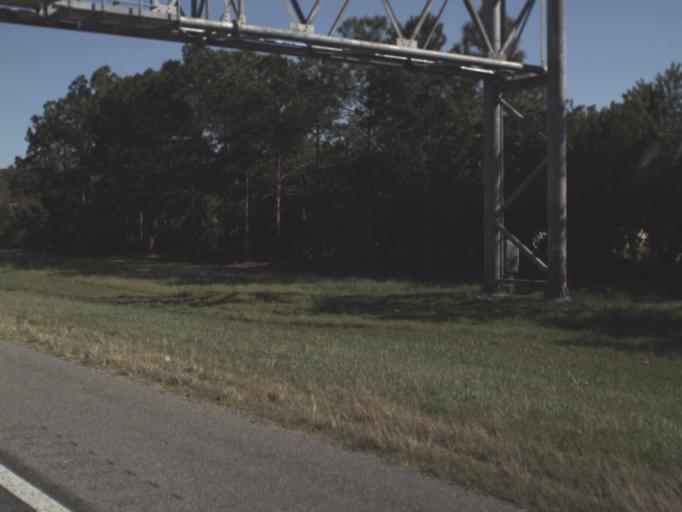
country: US
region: Florida
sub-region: Orange County
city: Williamsburg
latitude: 28.4211
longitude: -81.4333
